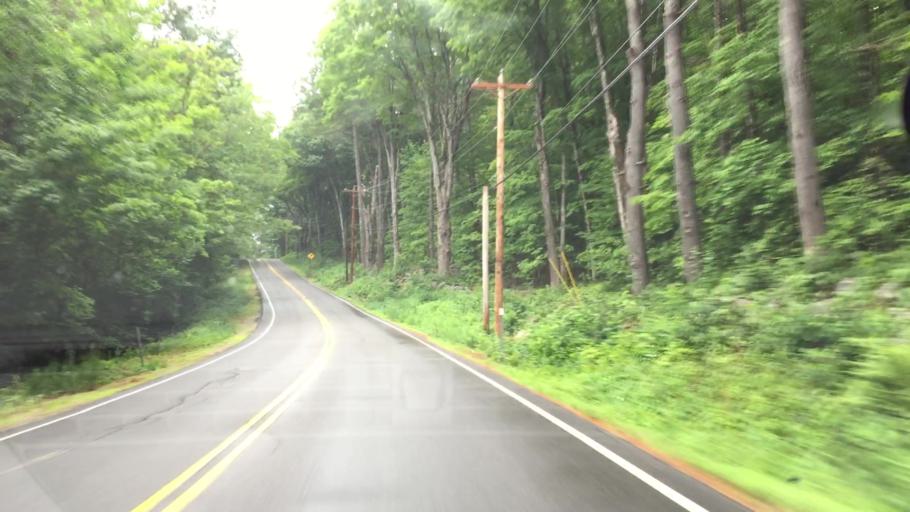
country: US
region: New Hampshire
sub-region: Carroll County
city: Center Harbor
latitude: 43.7580
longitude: -71.4818
